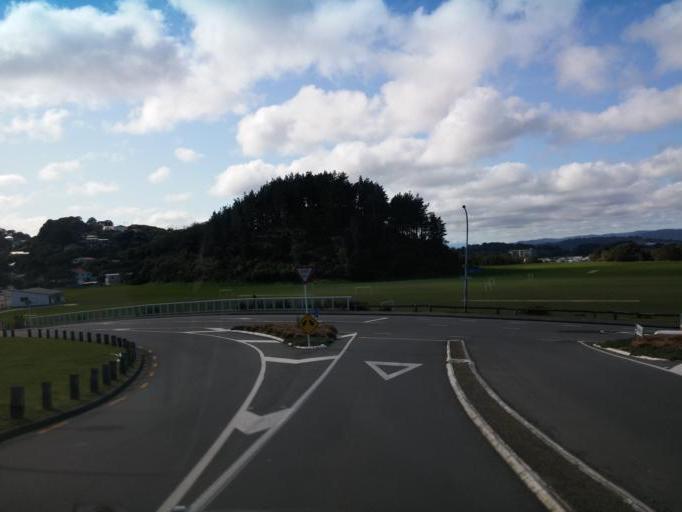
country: NZ
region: Wellington
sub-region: Wellington City
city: Brooklyn
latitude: -41.3193
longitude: 174.7695
